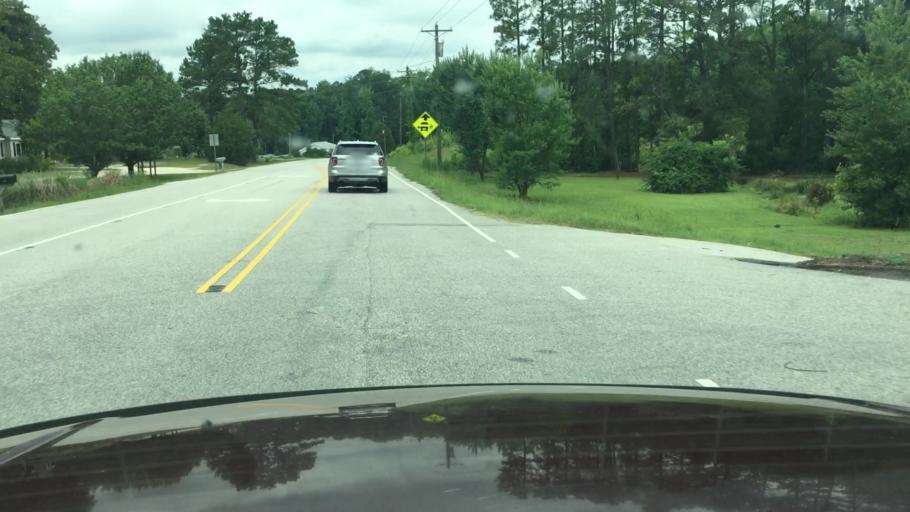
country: US
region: North Carolina
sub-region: Cumberland County
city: Spring Lake
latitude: 35.2564
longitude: -78.9746
